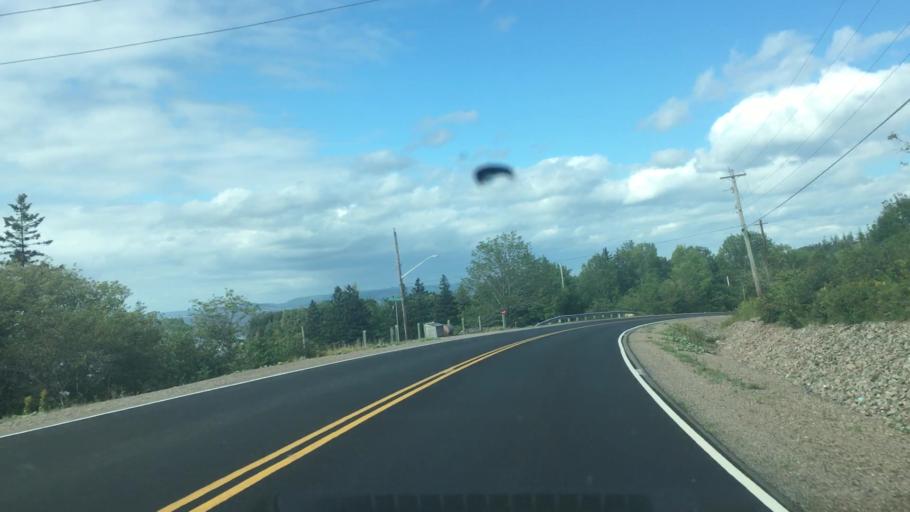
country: CA
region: Nova Scotia
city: Princeville
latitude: 45.7903
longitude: -60.7403
